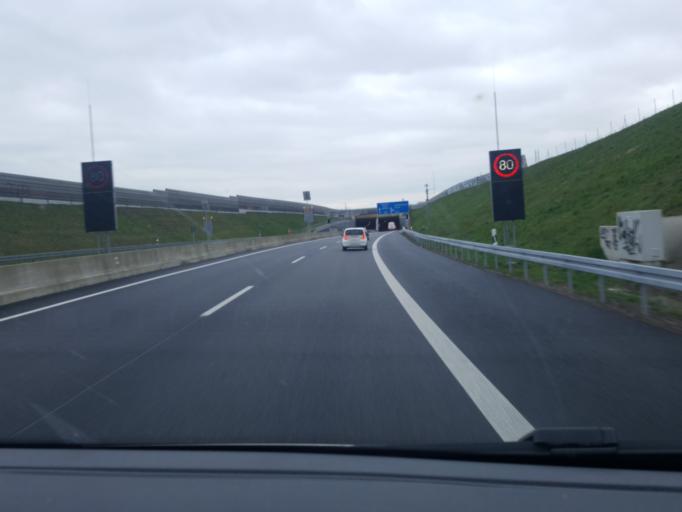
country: DE
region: North Rhine-Westphalia
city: Bad Oeynhausen
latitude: 52.2282
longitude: 8.8203
